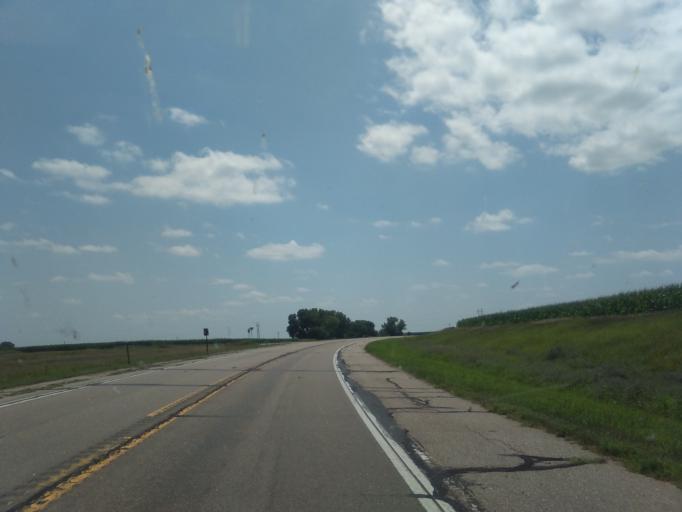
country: US
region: Nebraska
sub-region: Dawson County
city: Lexington
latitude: 40.6886
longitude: -99.7953
